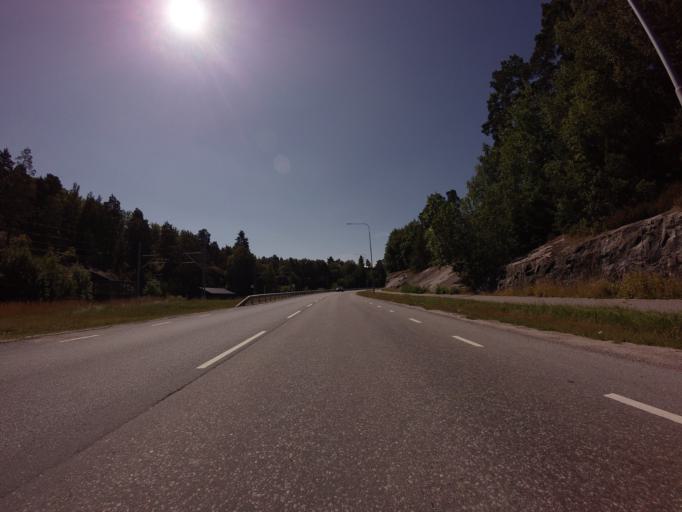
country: SE
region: Stockholm
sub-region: Lidingo
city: Brevik
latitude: 59.3551
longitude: 18.2217
